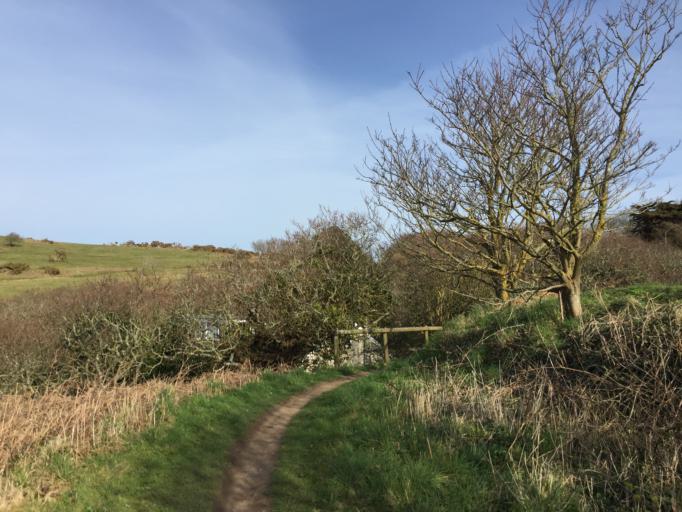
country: JE
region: St Helier
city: Saint Helier
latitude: 49.2510
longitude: -2.1712
